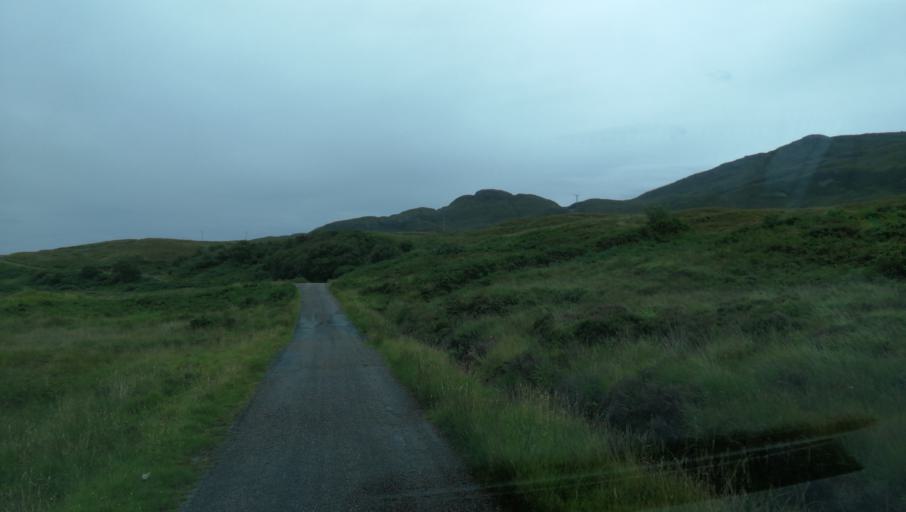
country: GB
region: Scotland
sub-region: Argyll and Bute
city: Isle Of Mull
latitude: 56.7149
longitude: -6.1482
